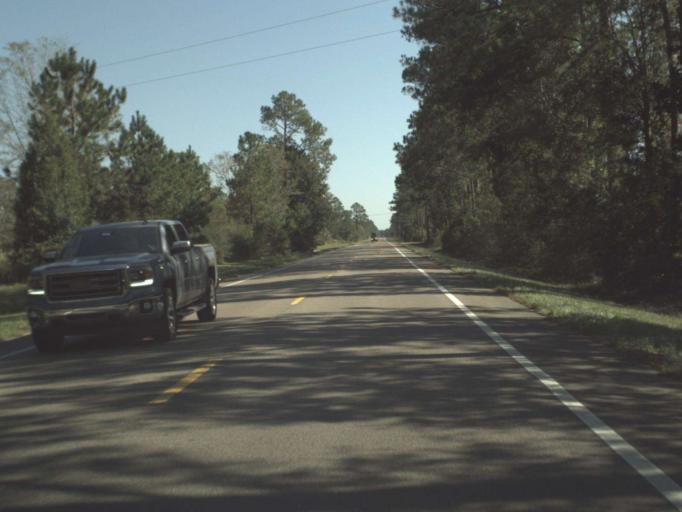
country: US
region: Florida
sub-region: Walton County
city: Freeport
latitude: 30.4833
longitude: -85.9529
